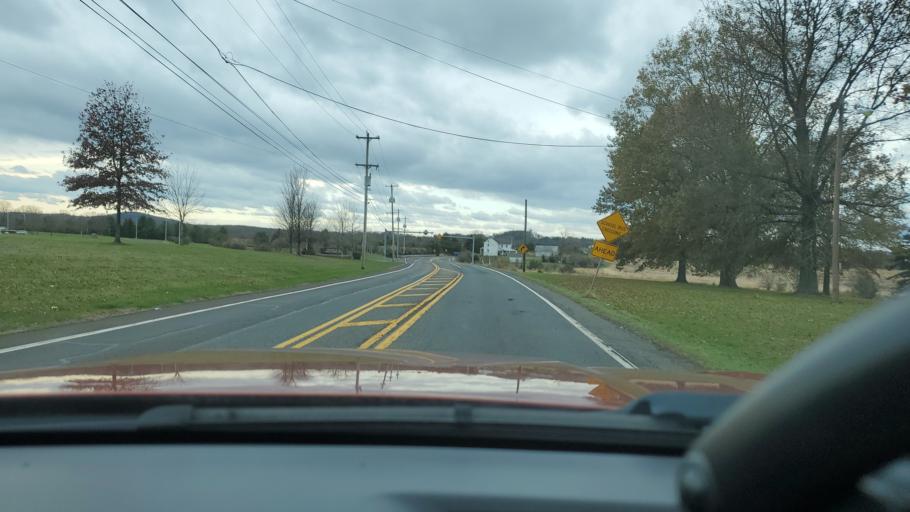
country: US
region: Pennsylvania
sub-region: Montgomery County
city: Spring Mount
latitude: 40.2790
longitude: -75.4939
